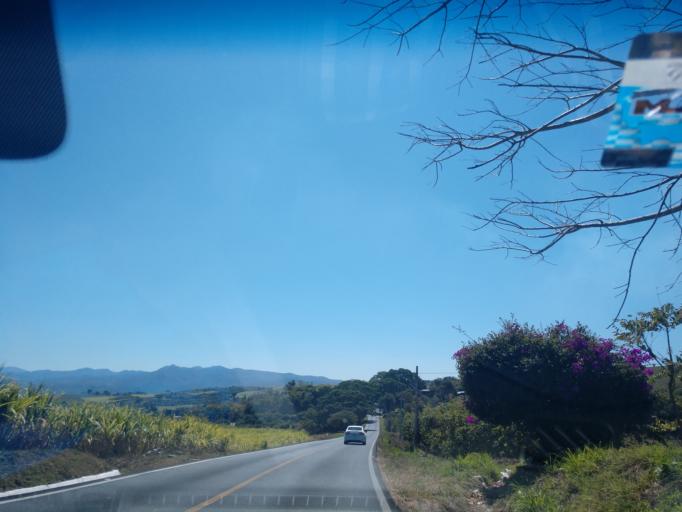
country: MX
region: Nayarit
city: Xalisco
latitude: 21.3876
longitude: -104.8905
